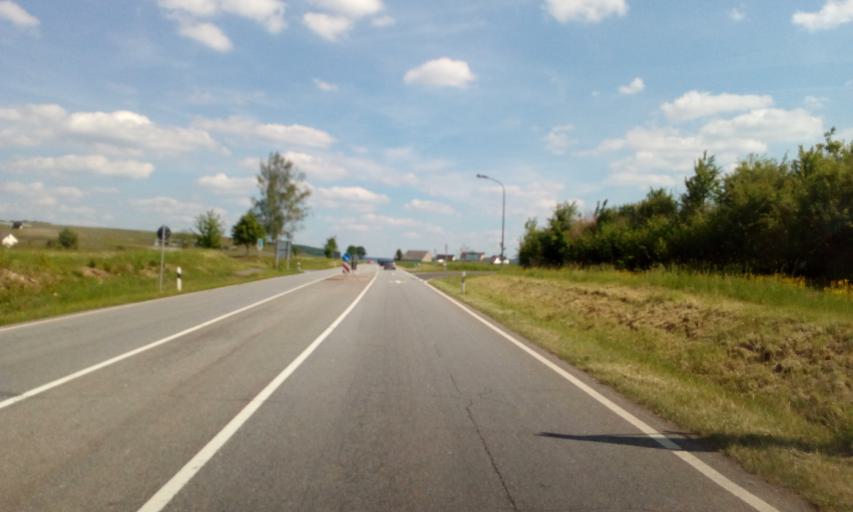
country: DE
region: Rheinland-Pfalz
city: Bekond
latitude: 49.8547
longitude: 6.8035
